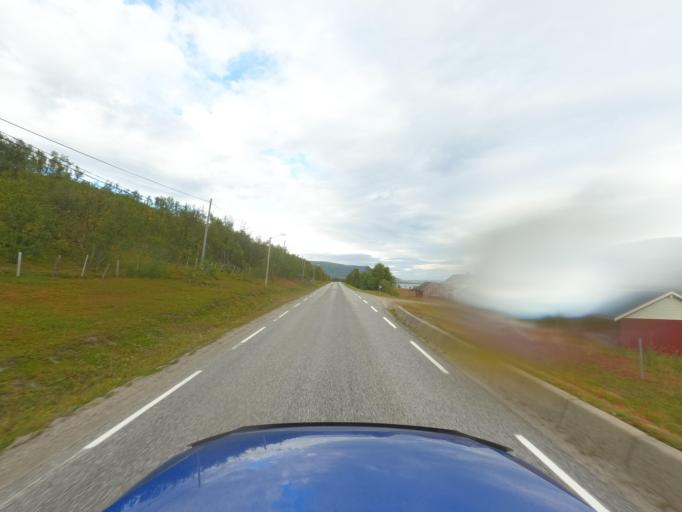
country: NO
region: Finnmark Fylke
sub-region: Porsanger
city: Lakselv
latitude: 70.5051
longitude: 25.0552
